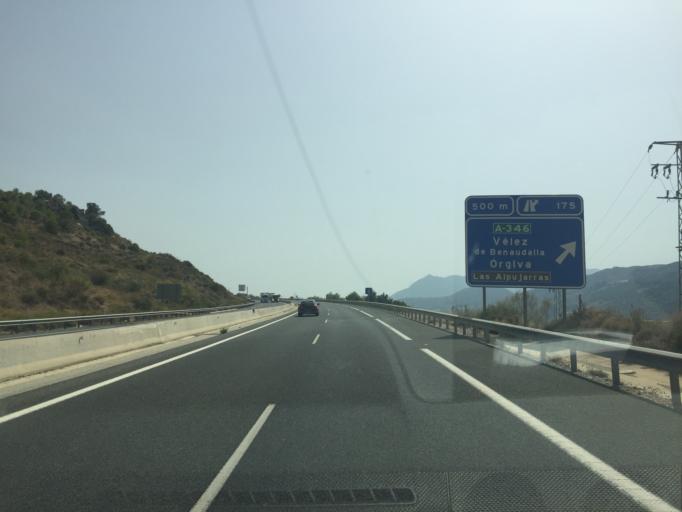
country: ES
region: Andalusia
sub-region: Provincia de Granada
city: Velez de Benaudalla
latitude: 36.8568
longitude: -3.4879
